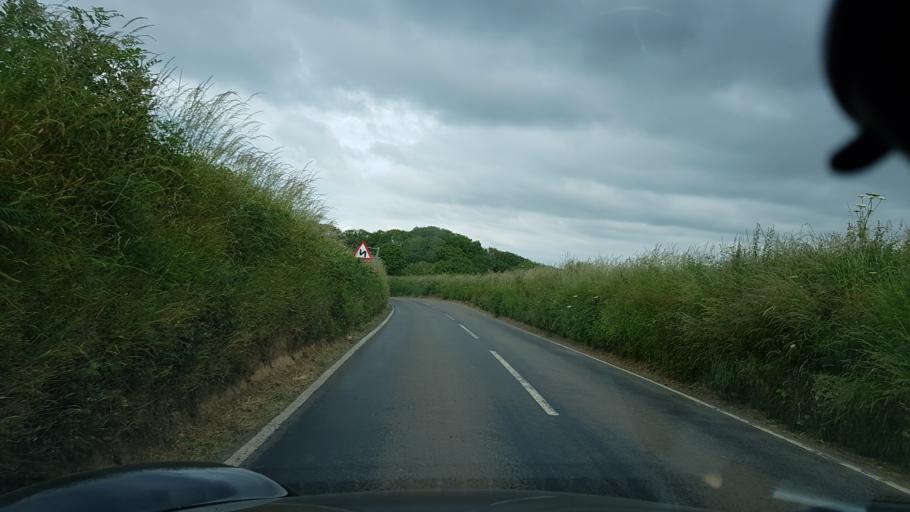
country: GB
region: Wales
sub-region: Pembrokeshire
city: Herbrandston
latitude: 51.7629
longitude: -5.0934
